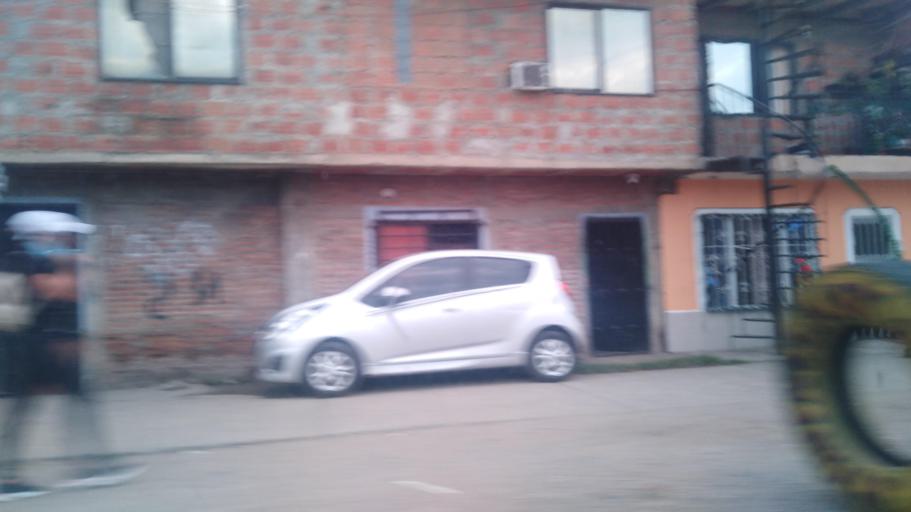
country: CO
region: Valle del Cauca
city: Cali
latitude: 3.4364
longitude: -76.4842
